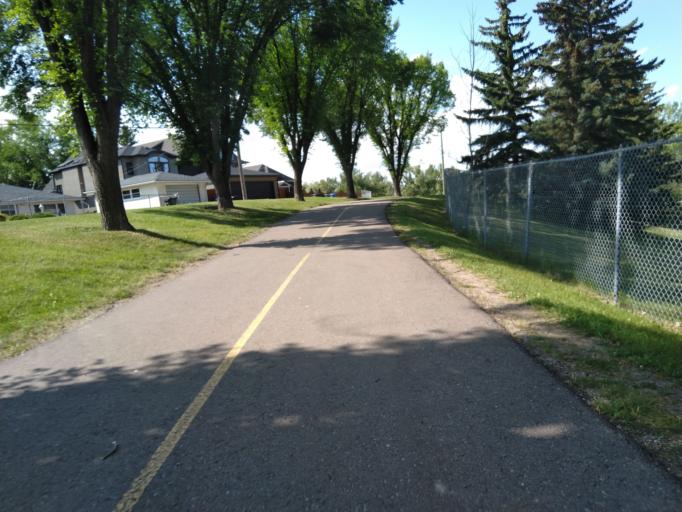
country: CA
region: Alberta
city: Calgary
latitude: 51.0774
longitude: -114.1039
